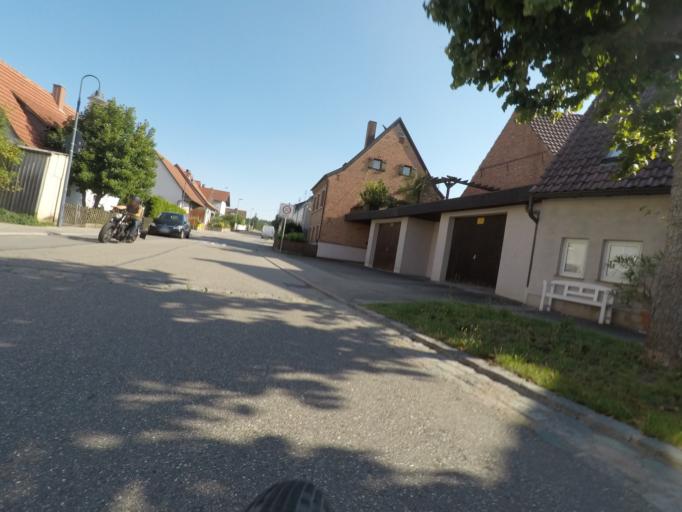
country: DE
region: Baden-Wuerttemberg
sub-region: Regierungsbezirk Stuttgart
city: Hildrizhausen
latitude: 48.6249
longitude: 8.9702
